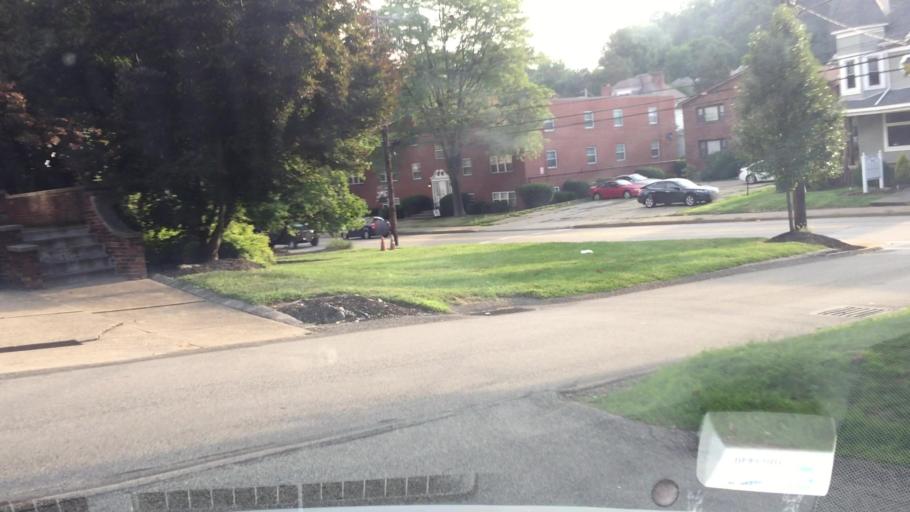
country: US
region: Pennsylvania
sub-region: Allegheny County
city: Carnegie
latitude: 40.4029
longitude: -80.0836
